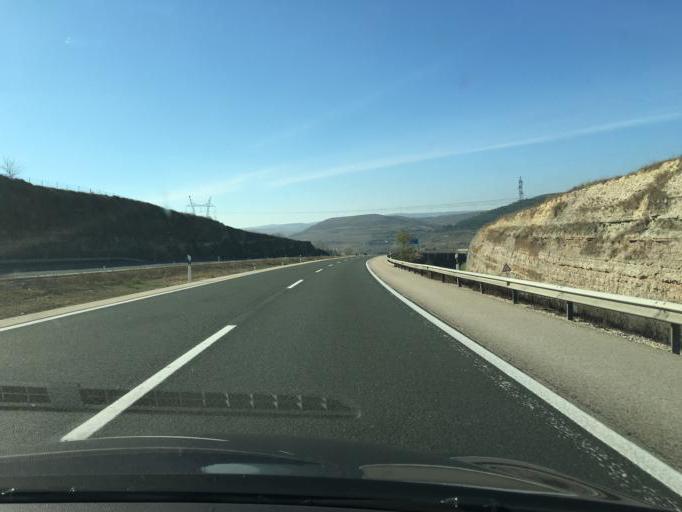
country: ES
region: Castille and Leon
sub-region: Provincia de Burgos
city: Briviesca
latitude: 42.5326
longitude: -3.3162
